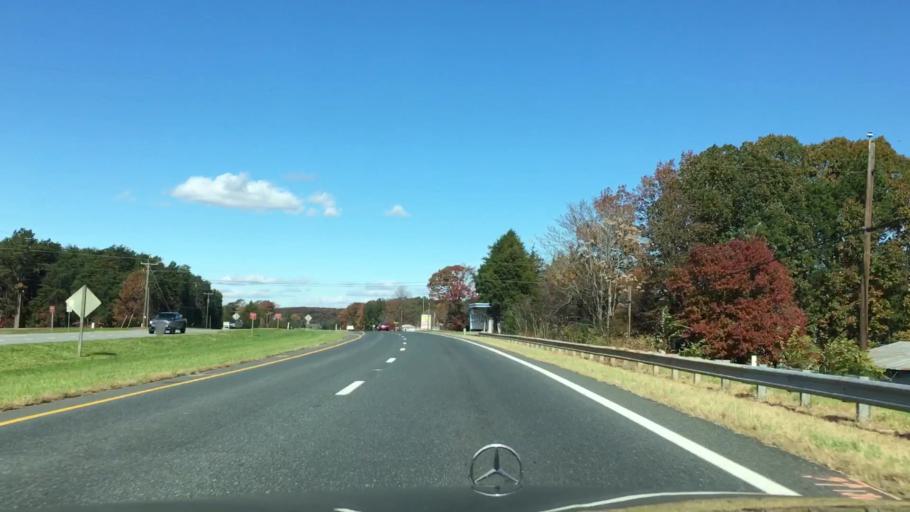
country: US
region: Virginia
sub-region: Campbell County
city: Rustburg
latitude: 37.2366
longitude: -79.1855
